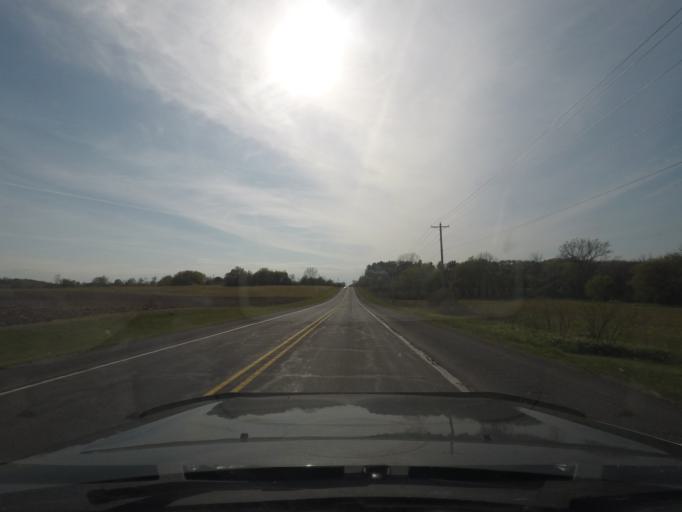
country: US
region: Indiana
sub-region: LaPorte County
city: Hudson Lake
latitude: 41.7981
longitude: -86.5068
